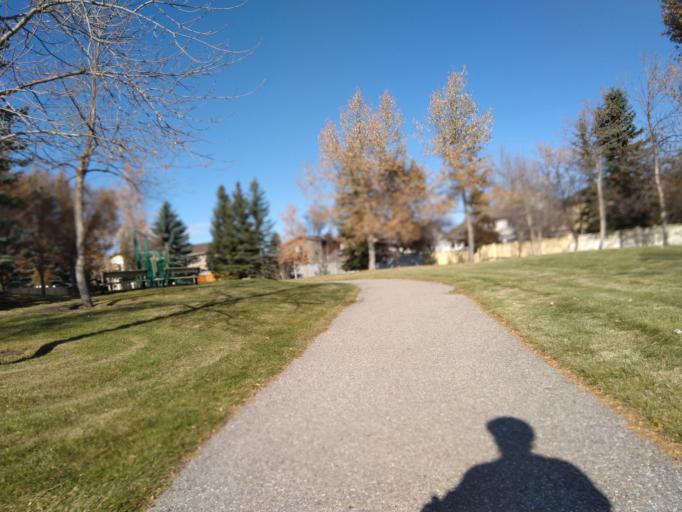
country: CA
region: Alberta
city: Calgary
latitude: 51.1361
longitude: -114.1539
